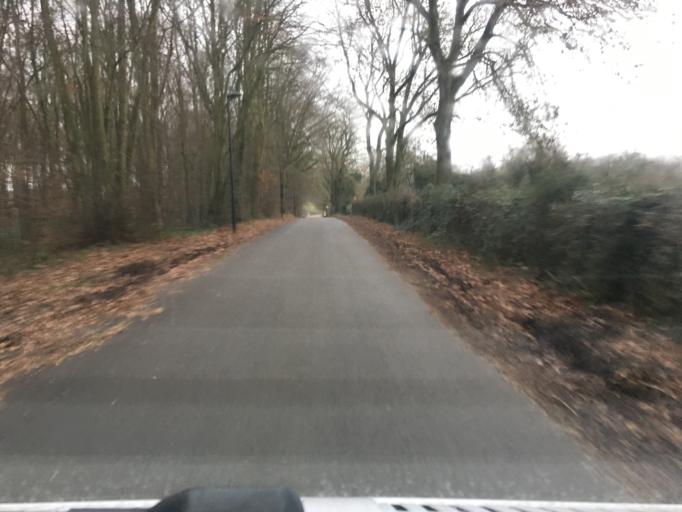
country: FR
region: Picardie
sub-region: Departement de la Somme
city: Saint-Valery-sur-Somme
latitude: 50.1761
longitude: 1.6380
